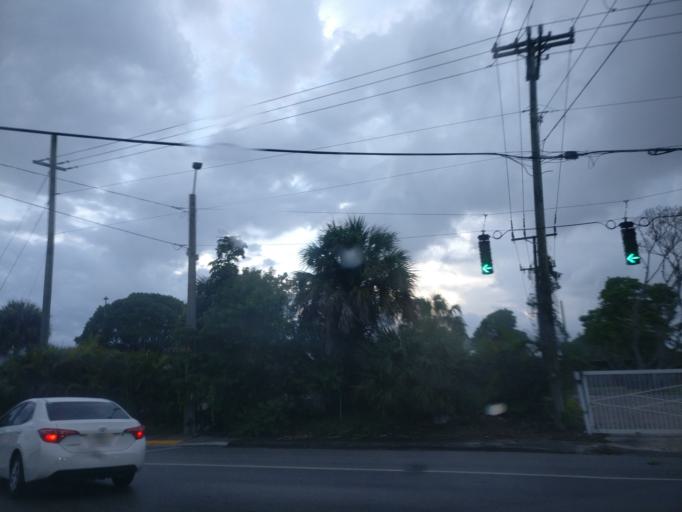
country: US
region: Florida
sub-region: Palm Beach County
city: Schall Circle
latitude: 26.7217
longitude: -80.1187
